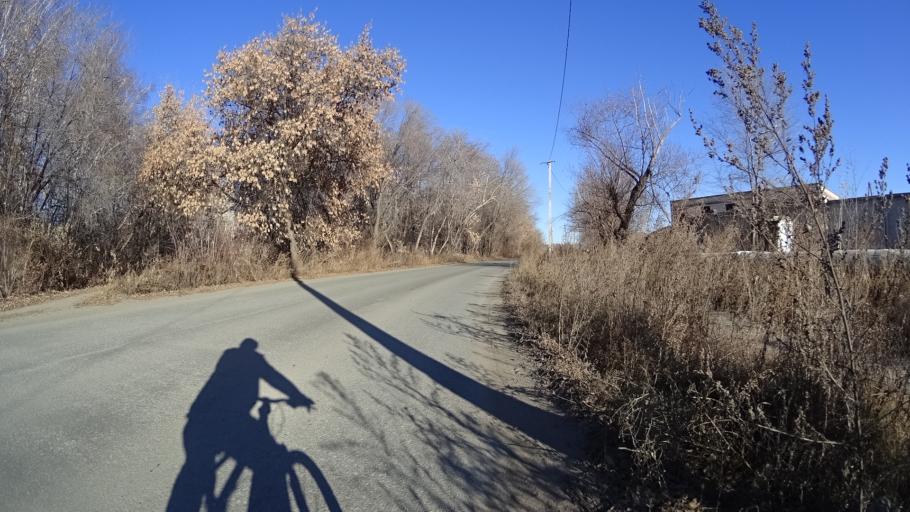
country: RU
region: Chelyabinsk
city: Troitsk
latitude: 54.0428
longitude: 61.6386
